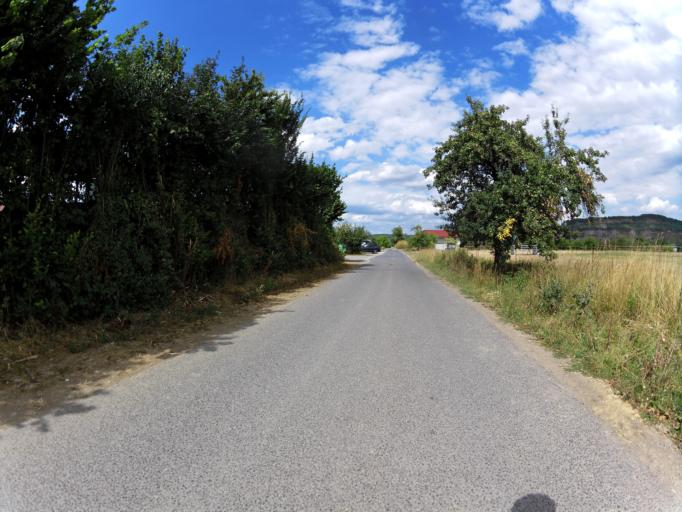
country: DE
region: Bavaria
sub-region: Regierungsbezirk Unterfranken
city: Zellingen
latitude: 49.8875
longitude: 9.8138
